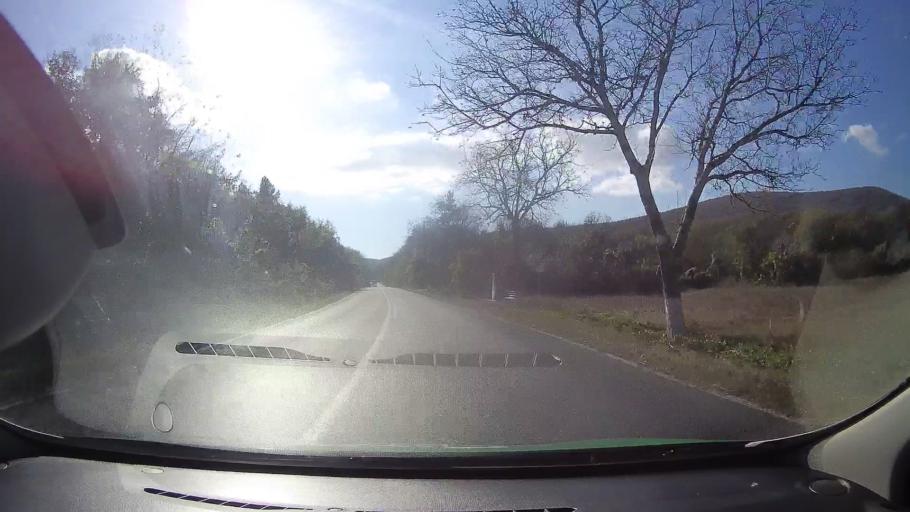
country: RO
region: Tulcea
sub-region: Oras Babadag
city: Babadag
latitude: 44.8739
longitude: 28.6889
